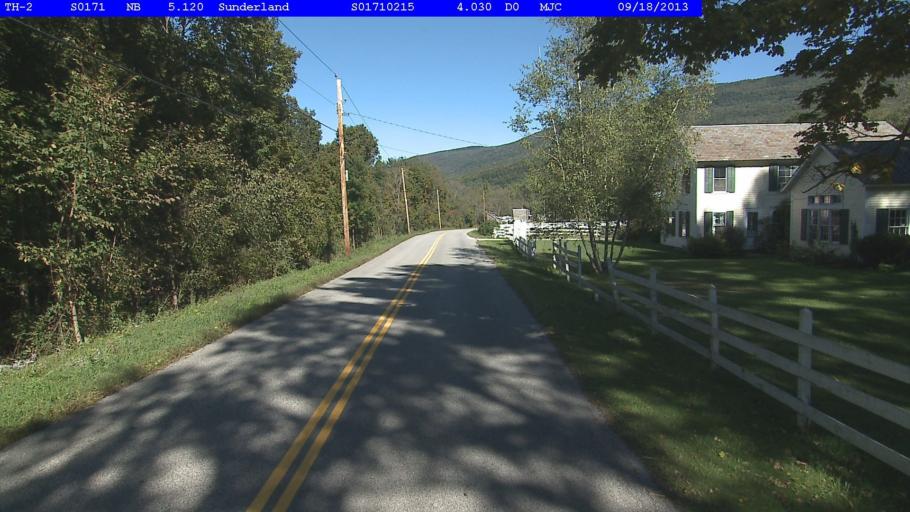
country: US
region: Vermont
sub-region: Bennington County
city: Arlington
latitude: 43.1137
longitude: -73.1026
